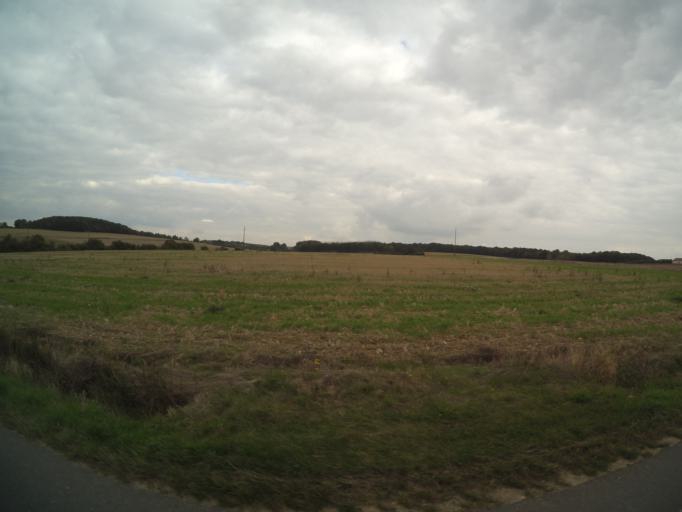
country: FR
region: Centre
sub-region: Departement d'Indre-et-Loire
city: Auzouer-en-Touraine
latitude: 47.5017
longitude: 0.9268
